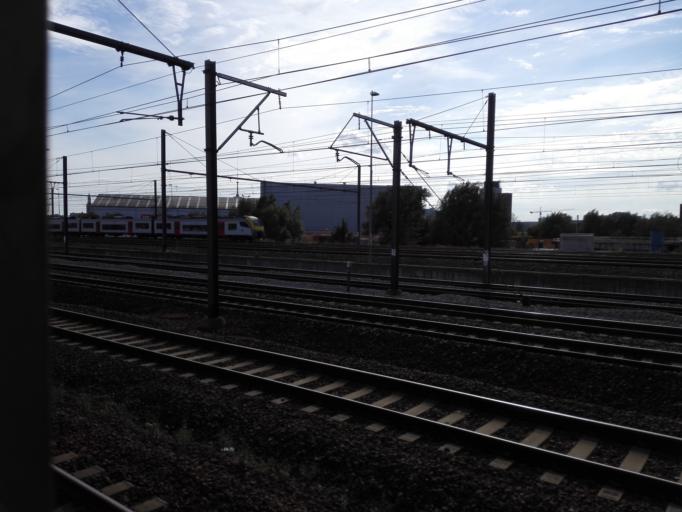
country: BE
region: Flanders
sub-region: Provincie Vlaams-Brabant
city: Leuven
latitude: 50.8907
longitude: 4.7138
